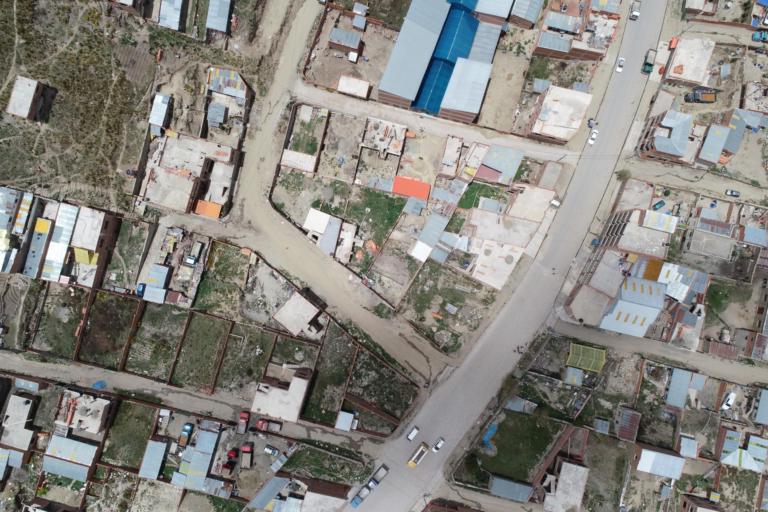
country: BO
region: La Paz
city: La Paz
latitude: -16.4412
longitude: -68.1438
